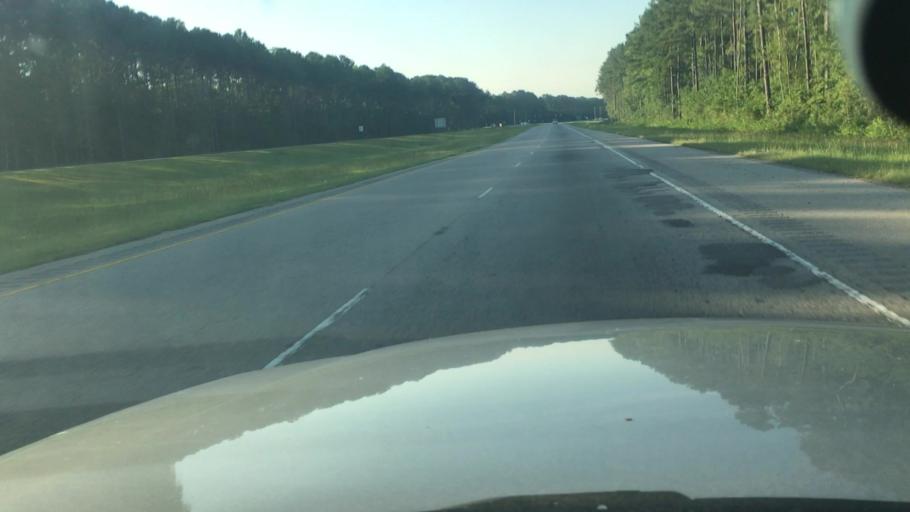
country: US
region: North Carolina
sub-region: Cumberland County
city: Vander
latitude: 34.9660
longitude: -78.8492
